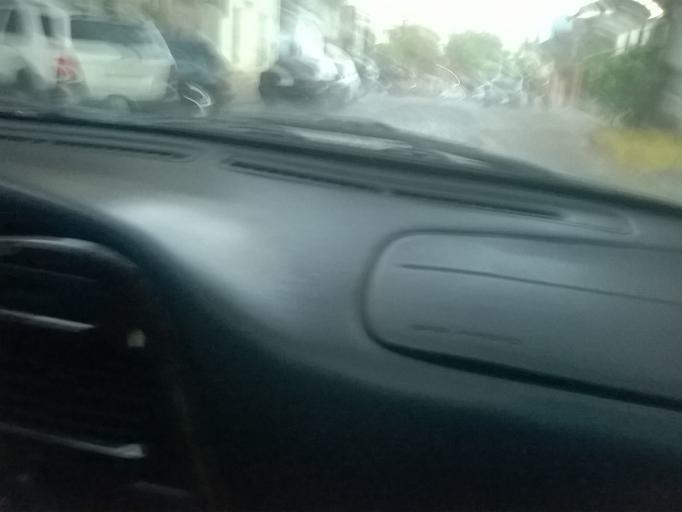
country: PY
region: Asuncion
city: Asuncion
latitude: -25.3068
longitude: -57.6011
